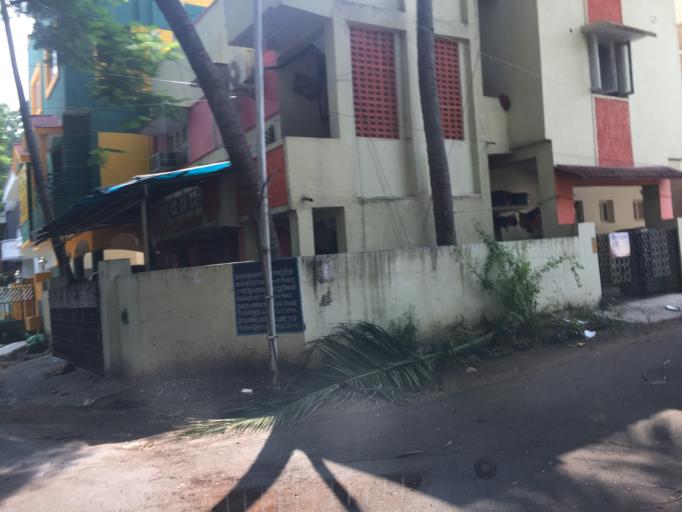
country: IN
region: Tamil Nadu
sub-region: Chennai
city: Gandhi Nagar
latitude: 13.0224
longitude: 80.2674
